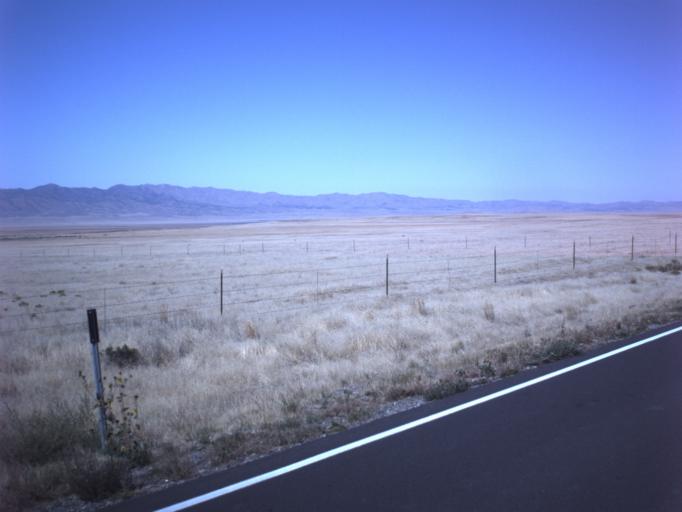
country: US
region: Utah
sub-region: Tooele County
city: Grantsville
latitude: 40.4039
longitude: -112.7481
